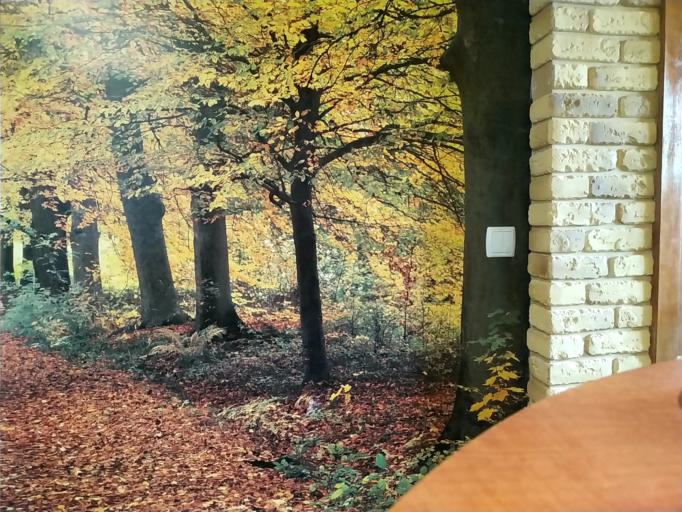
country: RU
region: Novgorod
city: Opechenskiy Posad
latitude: 58.2669
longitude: 34.0277
